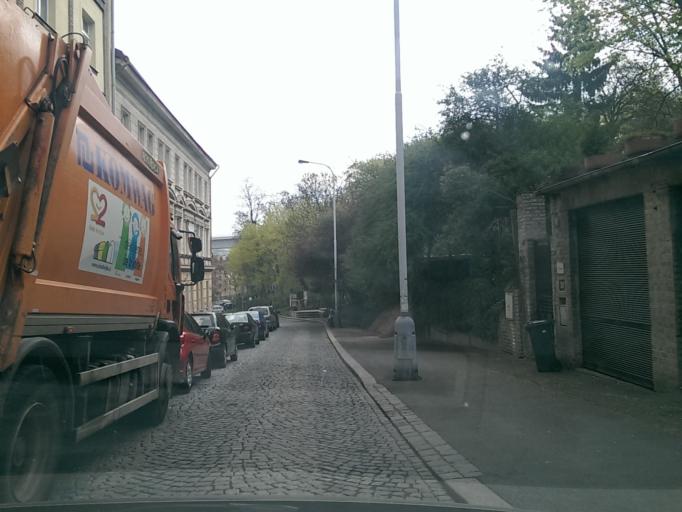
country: CZ
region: Praha
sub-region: Praha 2
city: Vysehrad
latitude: 50.0631
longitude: 14.4255
